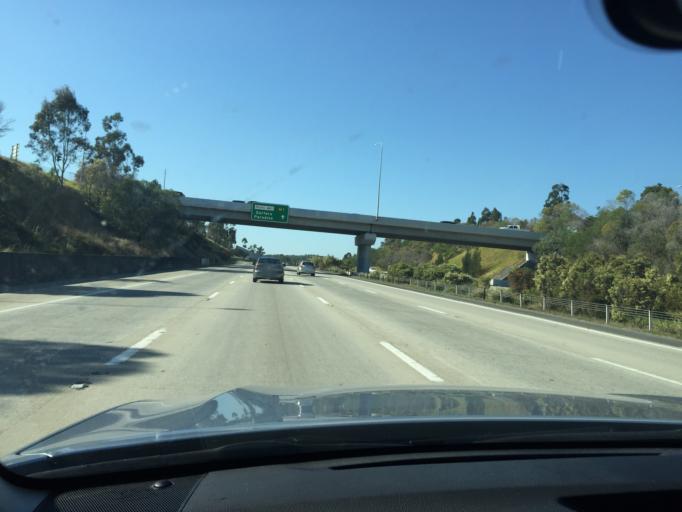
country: AU
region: Queensland
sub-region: Gold Coast
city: Ormeau Hills
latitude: -27.7856
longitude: 153.2560
